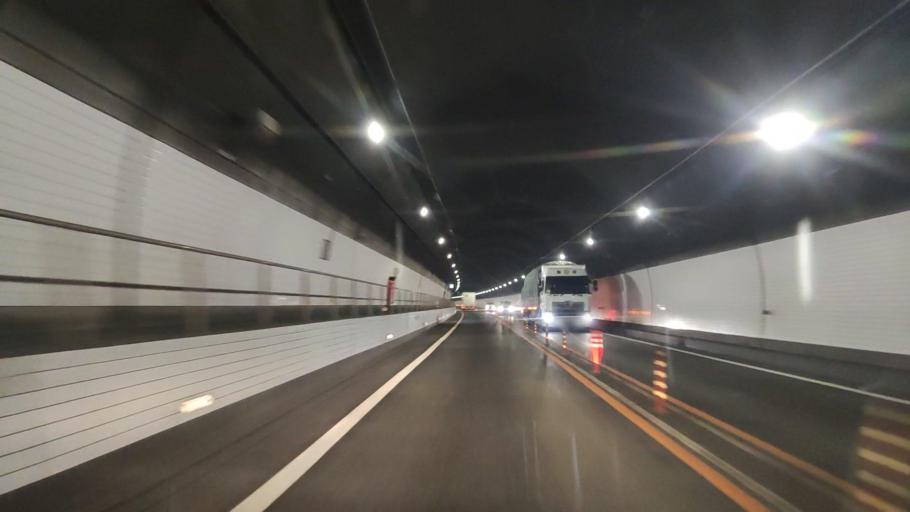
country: JP
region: Fukushima
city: Kitakata
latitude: 37.5991
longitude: 139.5554
